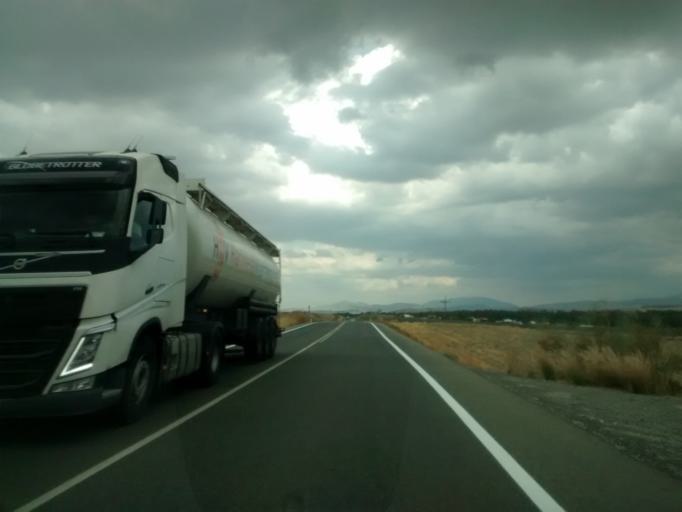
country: ES
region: Andalusia
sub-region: Provincia de Cadiz
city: Bornos
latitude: 36.8274
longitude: -5.7319
